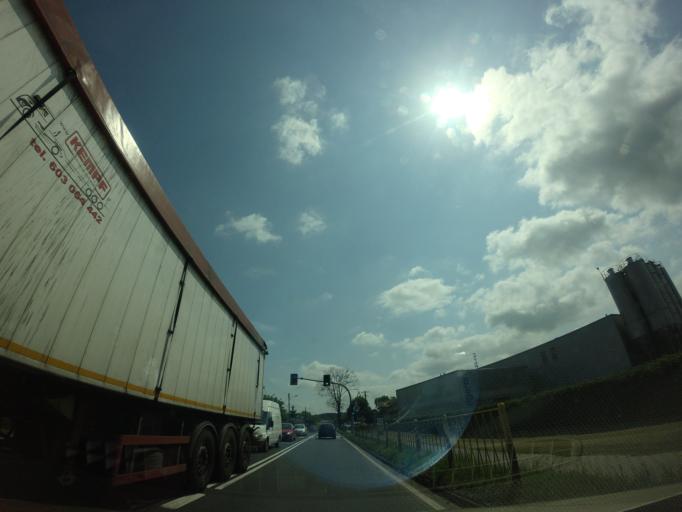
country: PL
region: West Pomeranian Voivodeship
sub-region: Powiat gryfinski
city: Stare Czarnowo
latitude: 53.3475
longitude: 14.7489
